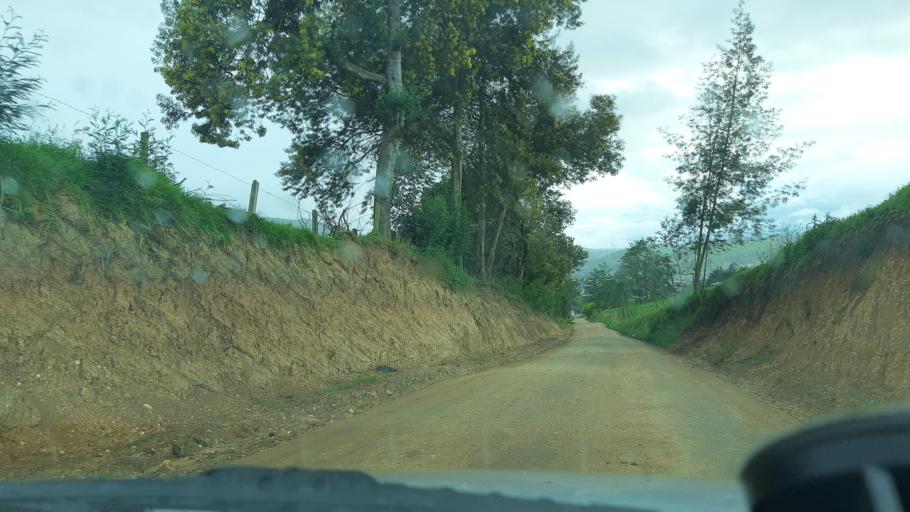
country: CO
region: Cundinamarca
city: Villapinzon
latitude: 5.2288
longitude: -73.5837
